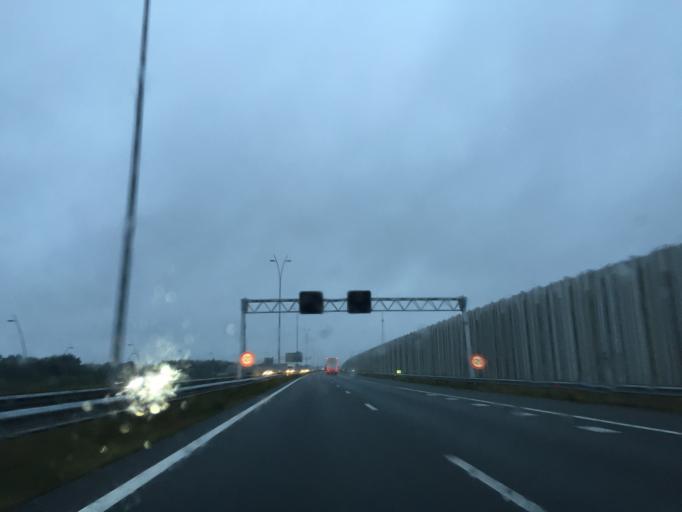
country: NL
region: North Brabant
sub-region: Gemeente Veldhoven
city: Veldhoven
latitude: 51.4127
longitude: 5.4299
